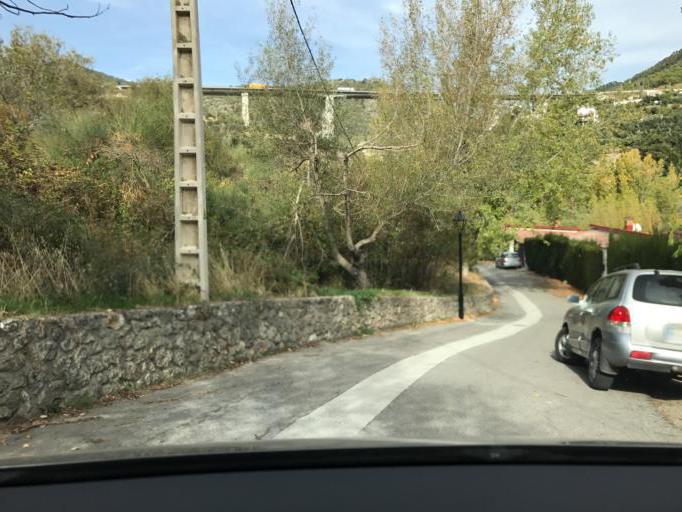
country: ES
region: Andalusia
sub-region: Provincia de Granada
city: Huetor Santillan
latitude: 37.2221
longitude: -3.5208
